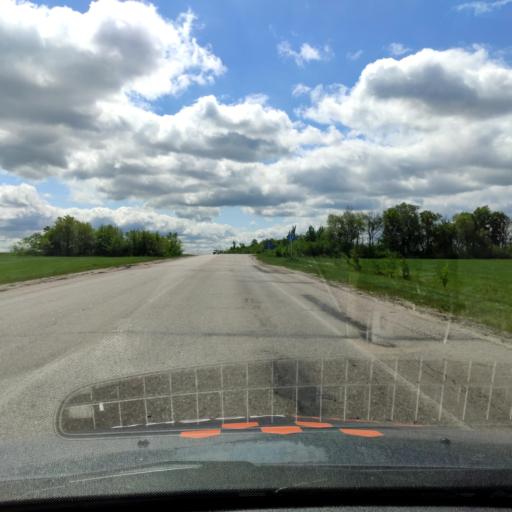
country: RU
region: Voronezj
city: Novaya Usman'
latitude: 51.5909
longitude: 39.3381
